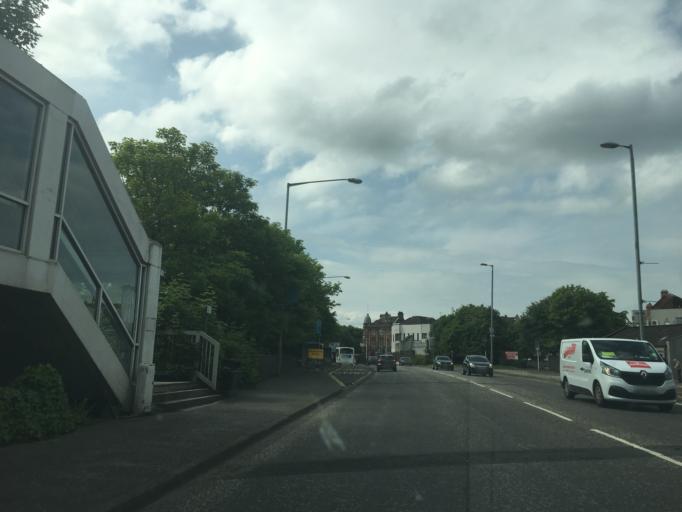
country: GB
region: Scotland
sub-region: North Lanarkshire
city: Coatbridge
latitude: 55.8612
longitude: -4.0267
